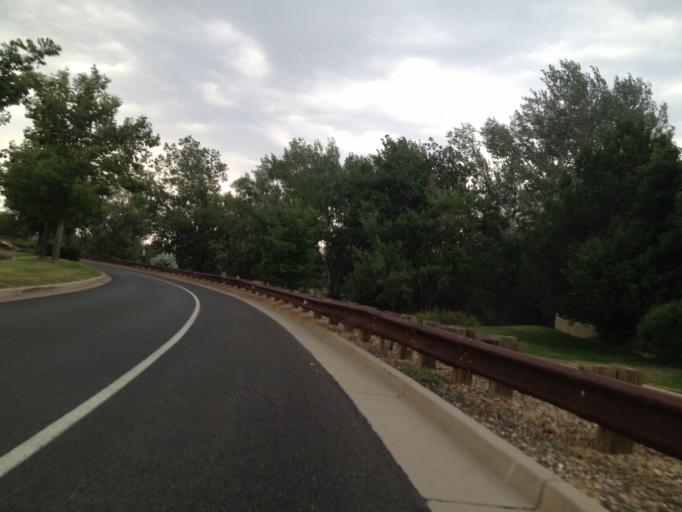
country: US
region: Colorado
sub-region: Boulder County
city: Louisville
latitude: 39.9651
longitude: -105.1433
